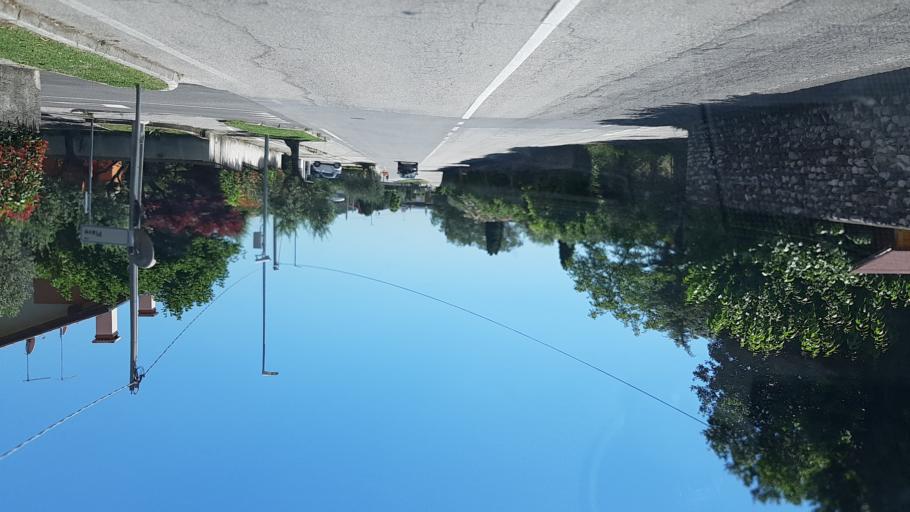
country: IT
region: Veneto
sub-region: Provincia di Vicenza
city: Pove del Grappa
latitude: 45.7915
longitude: 11.7342
